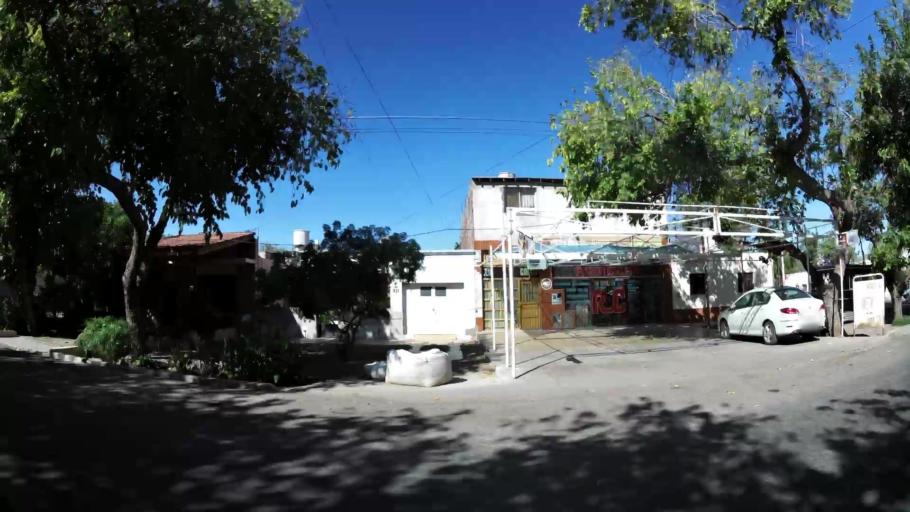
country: AR
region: San Juan
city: San Juan
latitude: -31.5302
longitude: -68.5357
